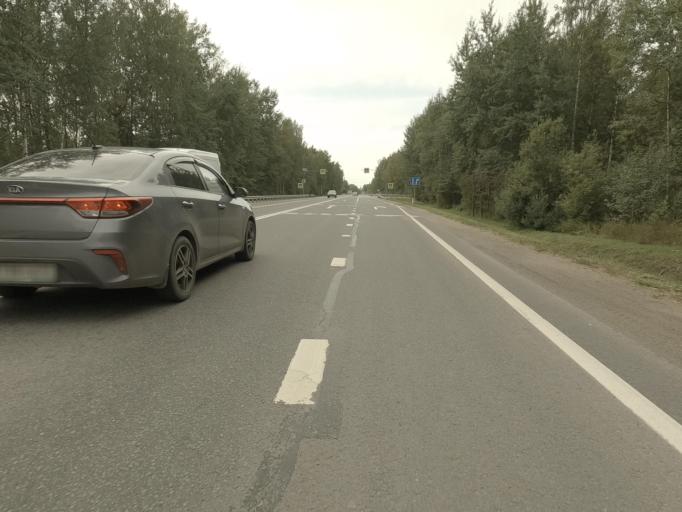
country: RU
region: Leningrad
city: Kirovsk
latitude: 59.8517
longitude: 31.0246
